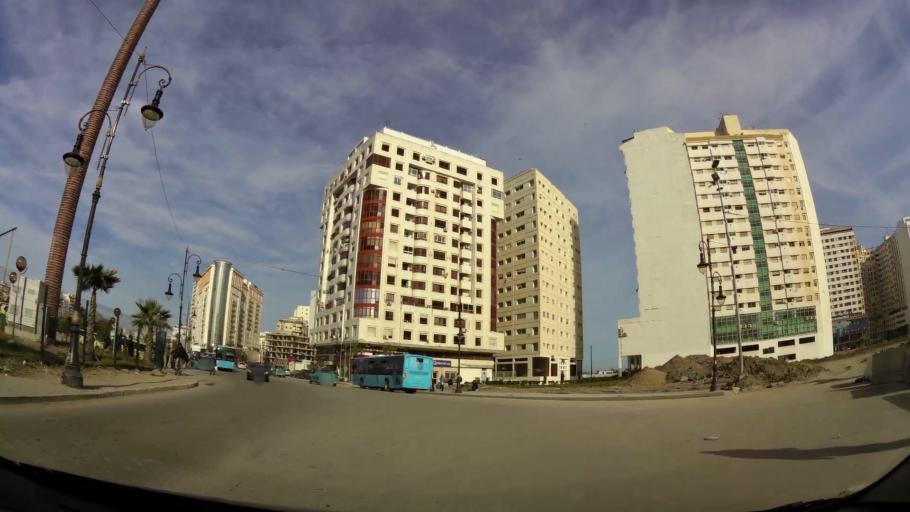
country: MA
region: Tanger-Tetouan
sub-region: Tanger-Assilah
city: Tangier
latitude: 35.7721
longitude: -5.7887
